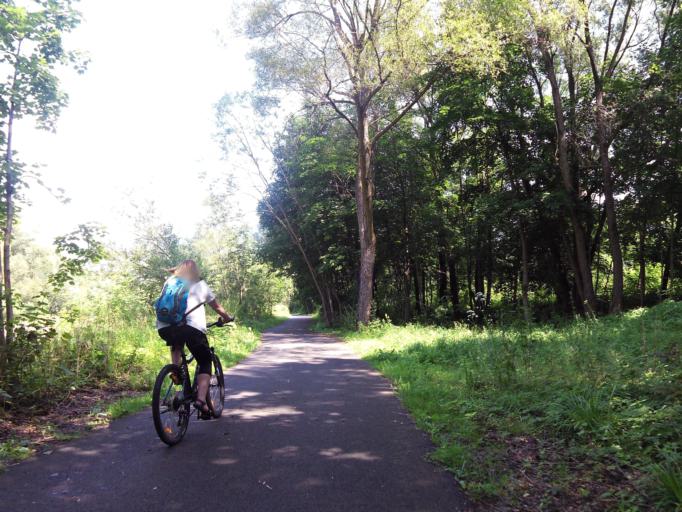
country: PL
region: Silesian Voivodeship
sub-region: Powiat zywiecki
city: Rajcza
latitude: 49.5104
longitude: 19.1135
